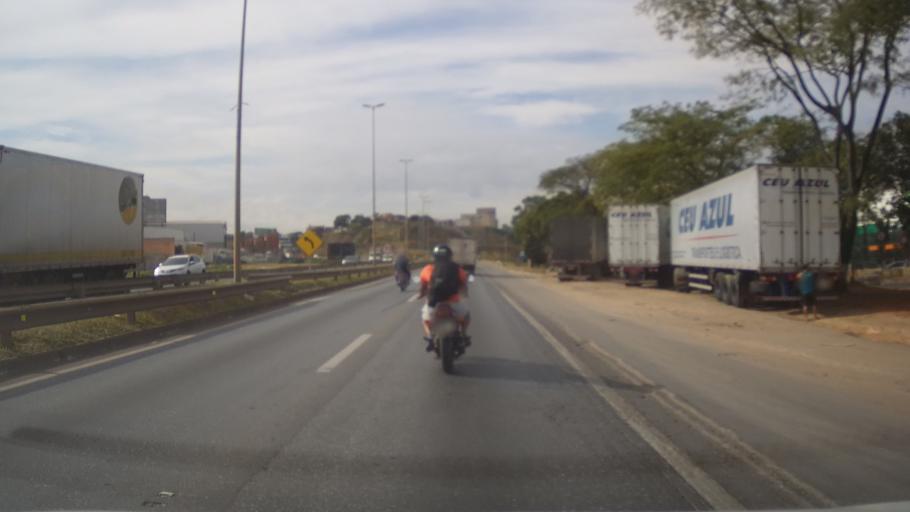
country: BR
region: Minas Gerais
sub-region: Contagem
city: Contagem
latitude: -19.9170
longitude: -44.0396
